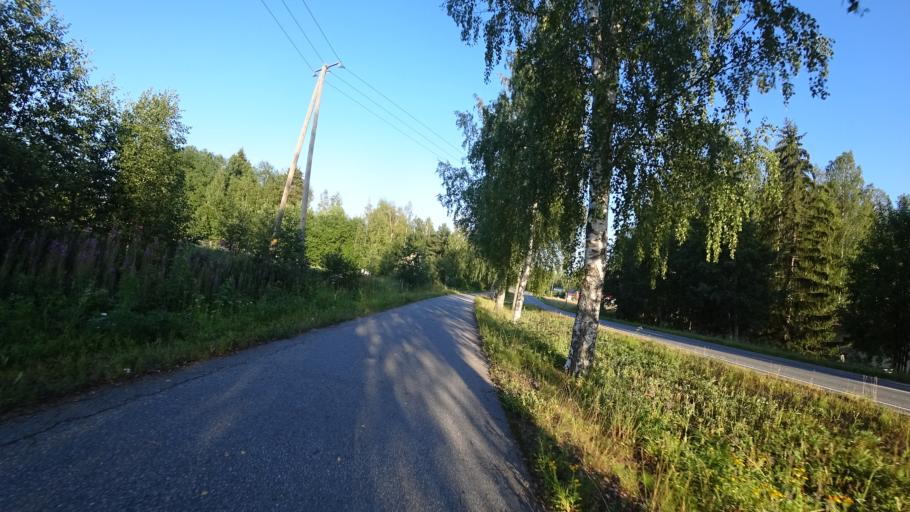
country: FI
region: Pirkanmaa
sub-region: Tampere
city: Nokia
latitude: 61.4695
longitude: 23.3938
